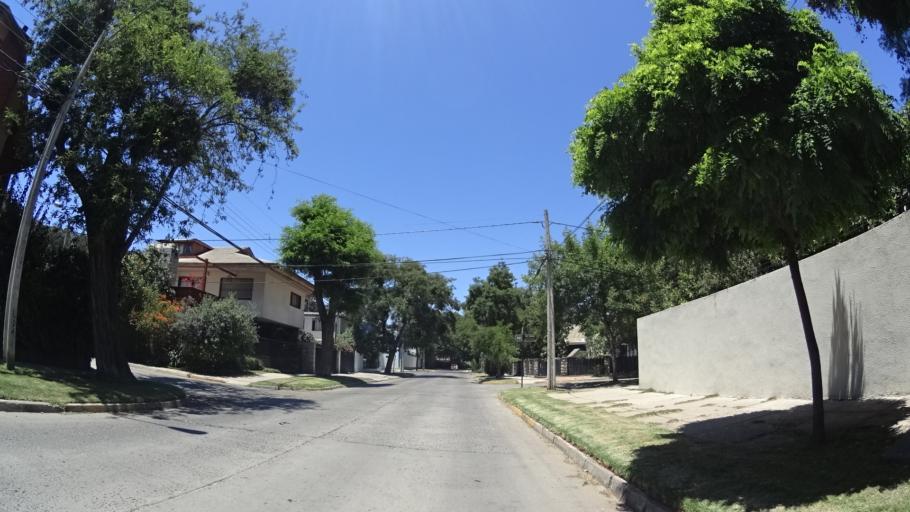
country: CL
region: Valparaiso
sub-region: Provincia de Valparaiso
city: Vina del Mar
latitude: -33.0273
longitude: -71.5327
